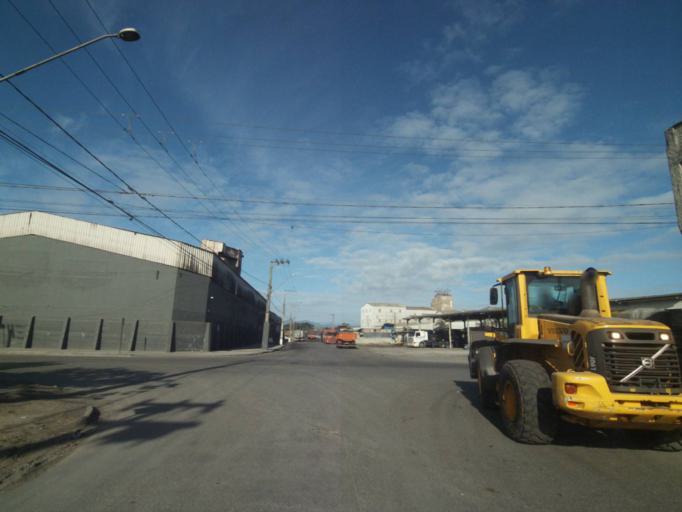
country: BR
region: Parana
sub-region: Paranagua
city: Paranagua
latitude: -25.5138
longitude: -48.5240
